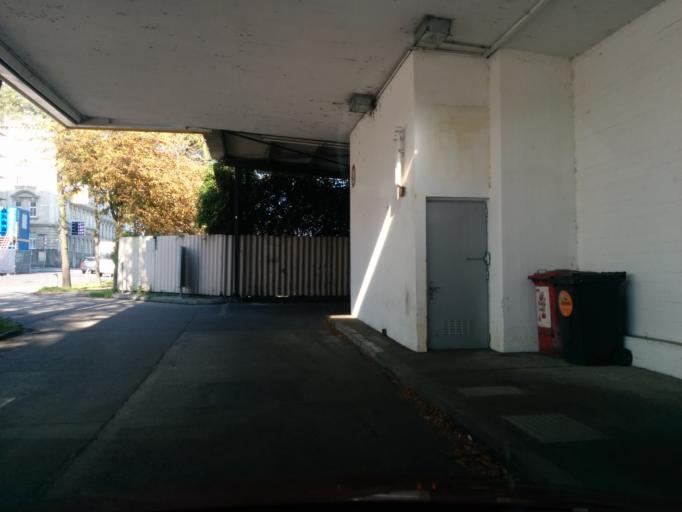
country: AT
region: Vienna
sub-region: Wien Stadt
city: Vienna
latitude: 48.1933
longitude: 16.3211
